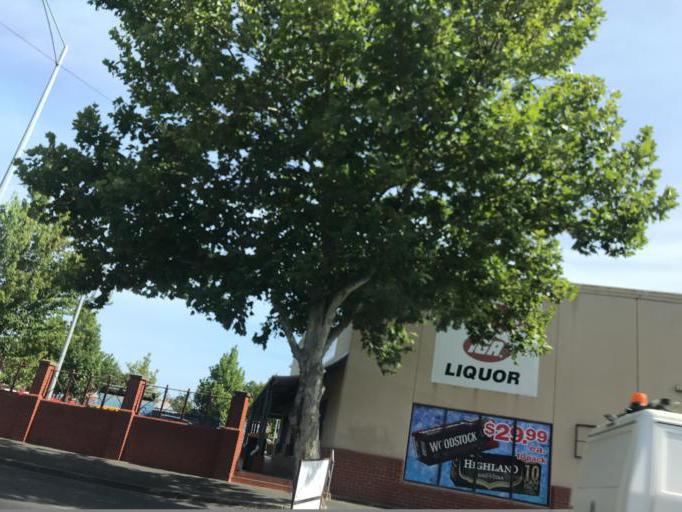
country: AU
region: Victoria
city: Ballarat East
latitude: -37.5610
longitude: 143.8687
